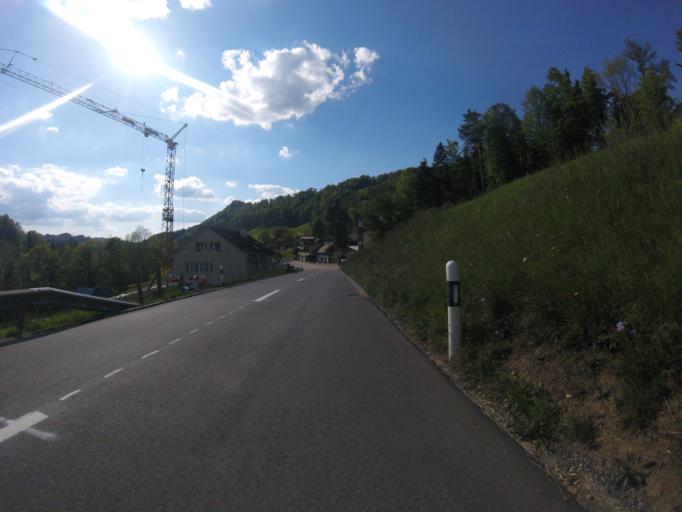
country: CH
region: Saint Gallen
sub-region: Wahlkreis Wil
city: Degersheim
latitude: 47.3623
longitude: 9.1757
